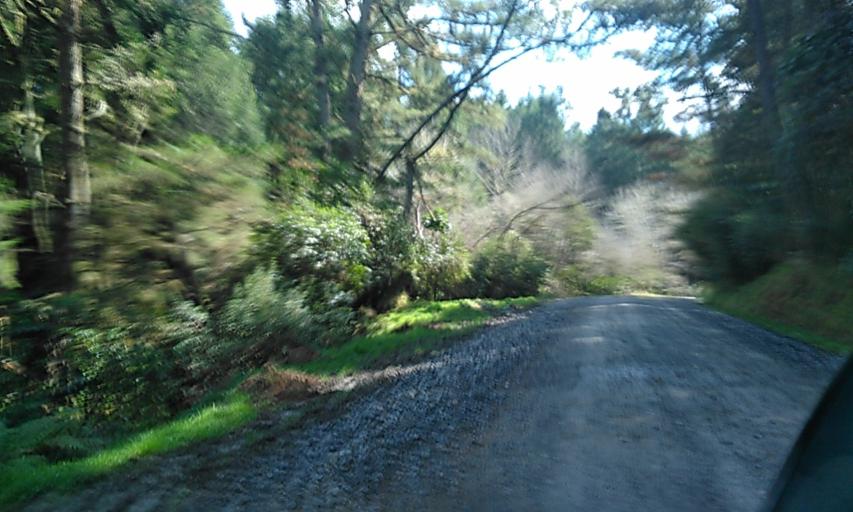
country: NZ
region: Gisborne
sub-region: Gisborne District
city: Gisborne
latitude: -38.2145
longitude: 178.0671
